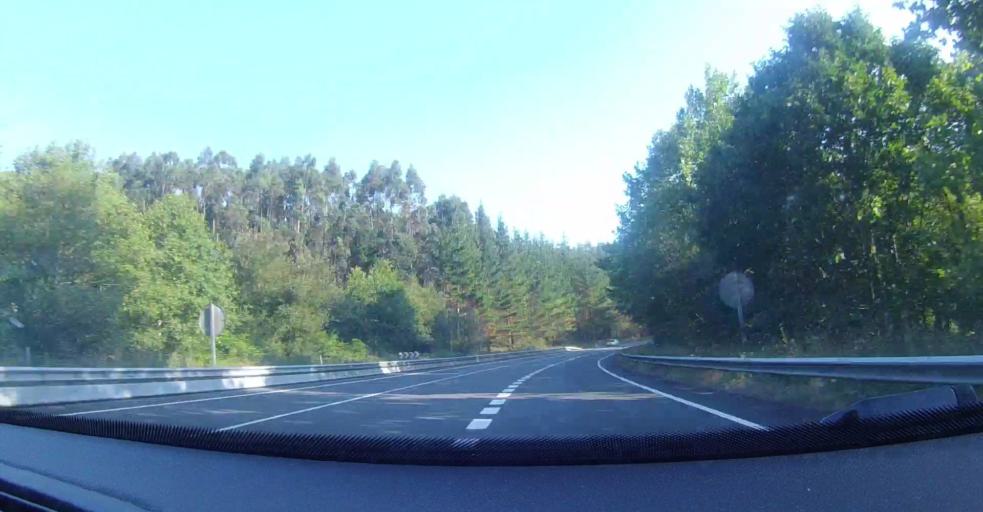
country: ES
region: Cantabria
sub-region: Provincia de Cantabria
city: Limpias
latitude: 43.3640
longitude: -3.4131
